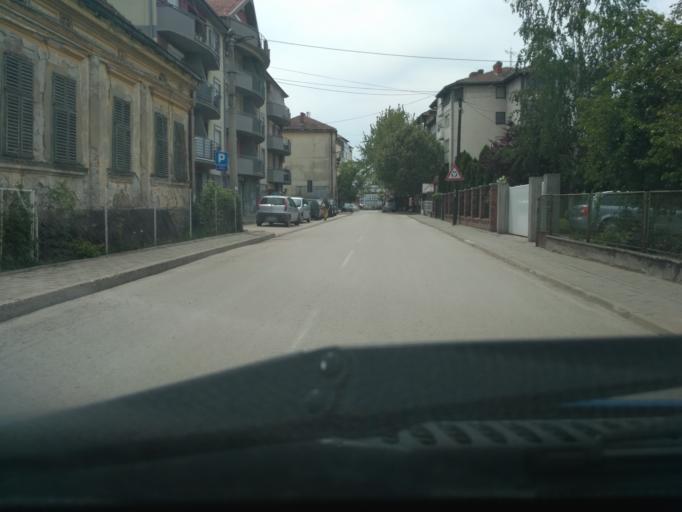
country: RS
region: Central Serbia
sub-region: Pomoravski Okrug
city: Svilajnac
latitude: 44.2312
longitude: 21.1992
